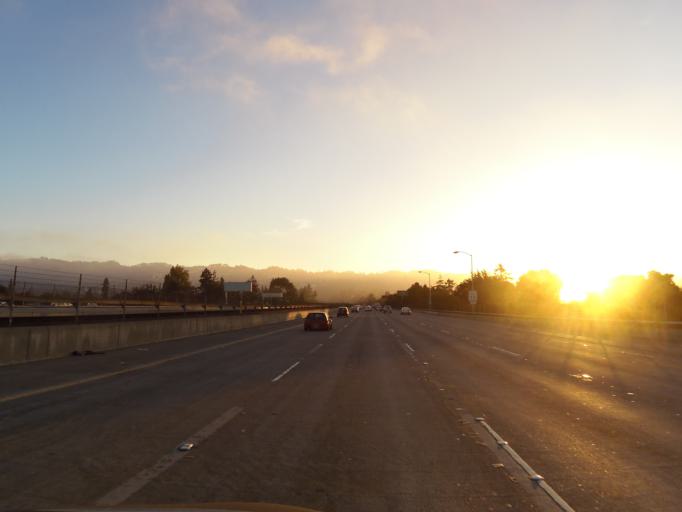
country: US
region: California
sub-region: Alameda County
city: Emeryville
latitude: 37.8421
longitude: -122.2585
